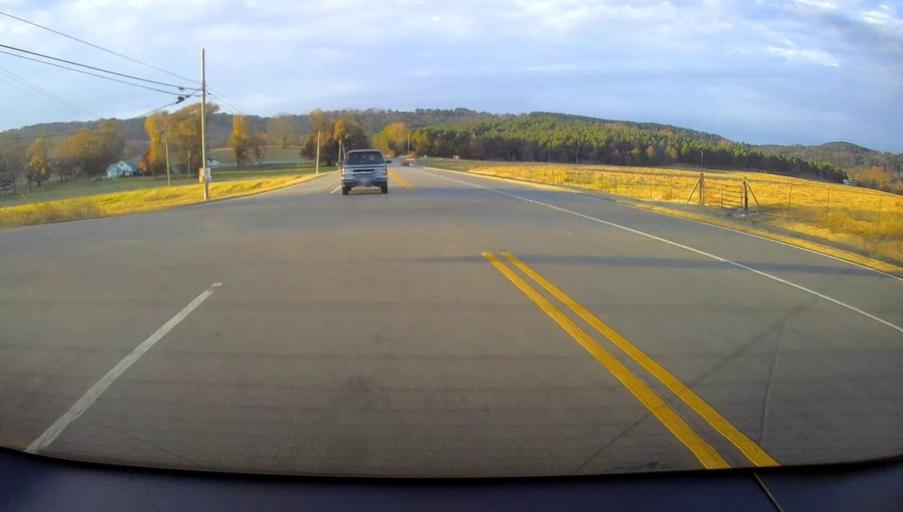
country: US
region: Alabama
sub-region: Etowah County
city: Attalla
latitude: 34.0472
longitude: -86.1578
